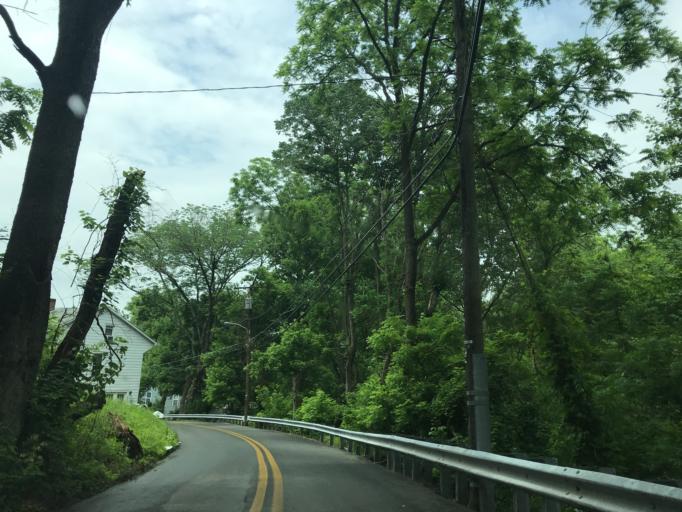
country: US
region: Maryland
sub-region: Howard County
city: Ellicott City
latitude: 39.2760
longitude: -76.7838
